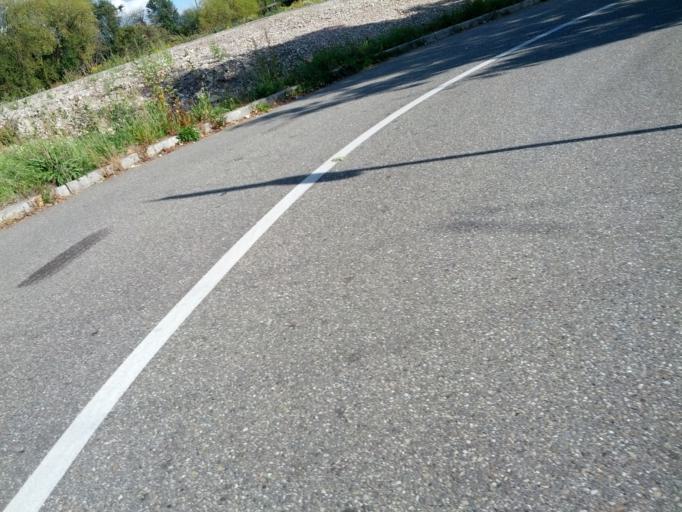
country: DE
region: Baden-Wuerttemberg
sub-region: Freiburg Region
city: Merzhausen
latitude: 47.9874
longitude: 7.8287
